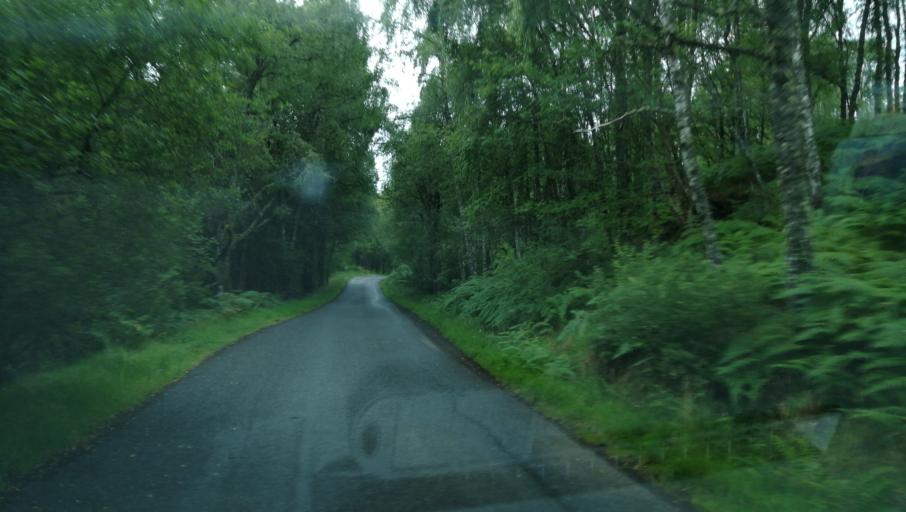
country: GB
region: Scotland
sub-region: Highland
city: Beauly
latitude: 57.3213
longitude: -4.8016
